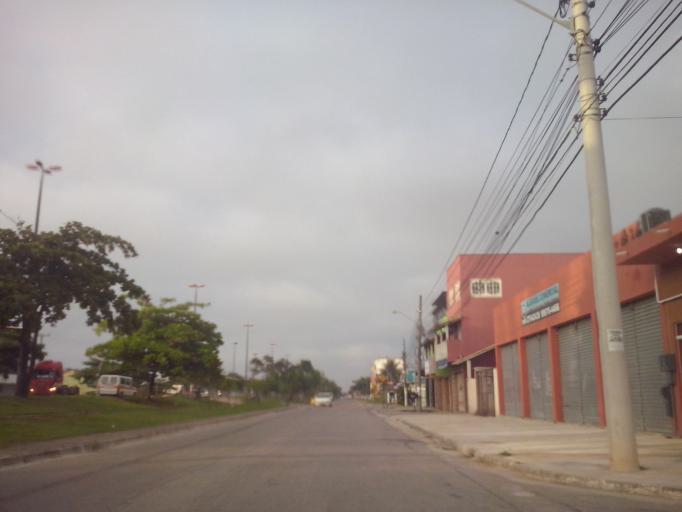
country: BR
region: Rio de Janeiro
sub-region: Rio Das Ostras
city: Rio das Ostras
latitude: -22.5496
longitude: -41.9753
